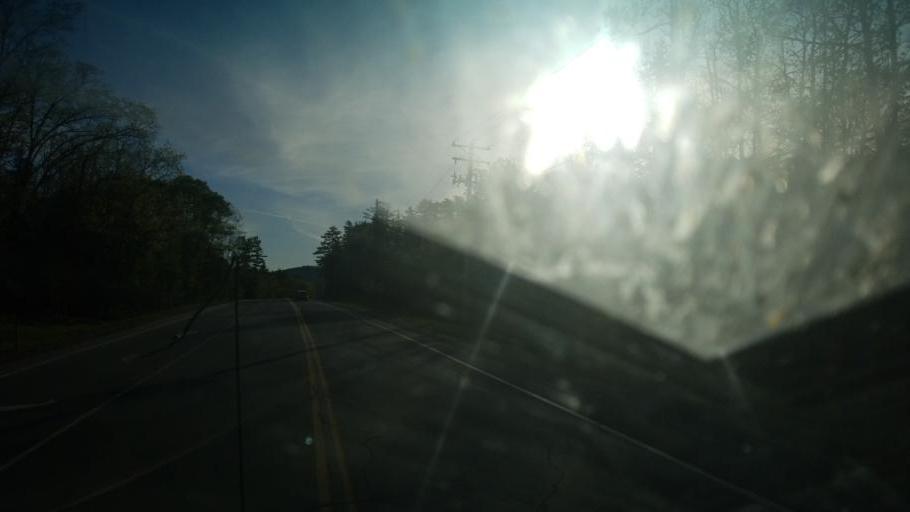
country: US
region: New Hampshire
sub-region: Grafton County
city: Littleton
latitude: 44.3163
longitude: -71.8251
